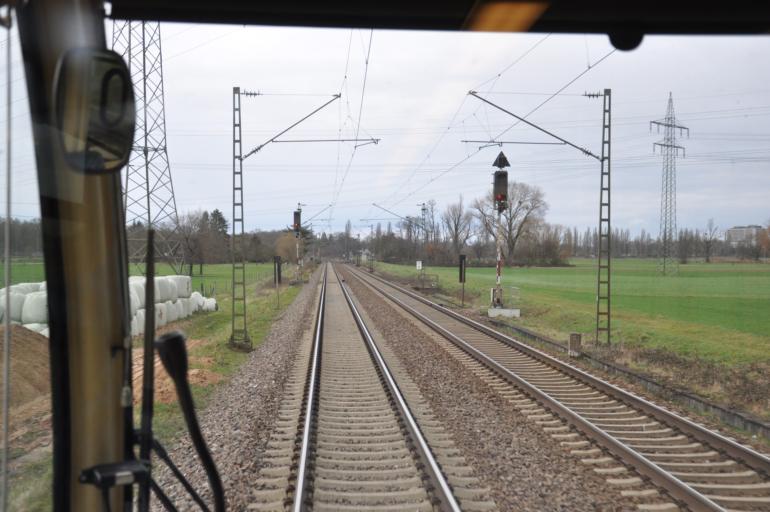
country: DE
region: Baden-Wuerttemberg
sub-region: Karlsruhe Region
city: Ettlingen
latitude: 48.9642
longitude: 8.3910
